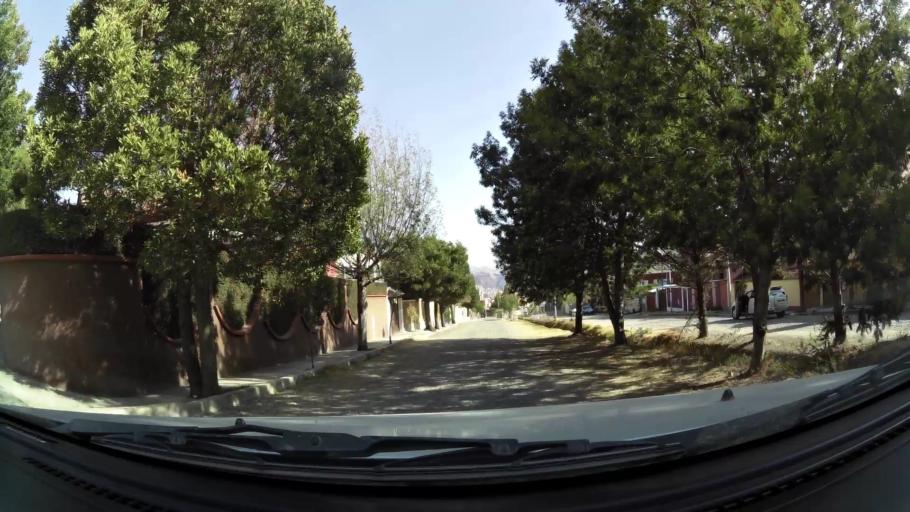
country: BO
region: La Paz
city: La Paz
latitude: -16.5277
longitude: -68.0736
